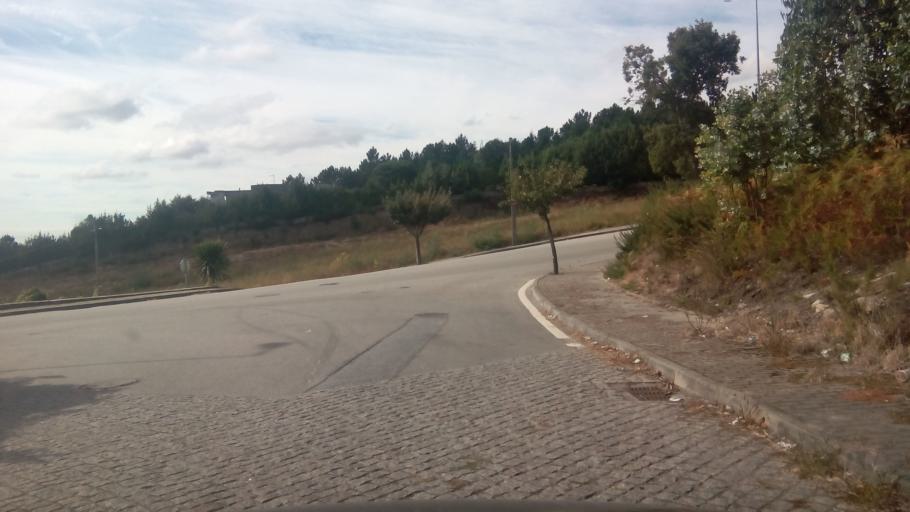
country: PT
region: Porto
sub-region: Paredes
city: Rebordosa
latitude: 41.1978
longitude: -8.4026
